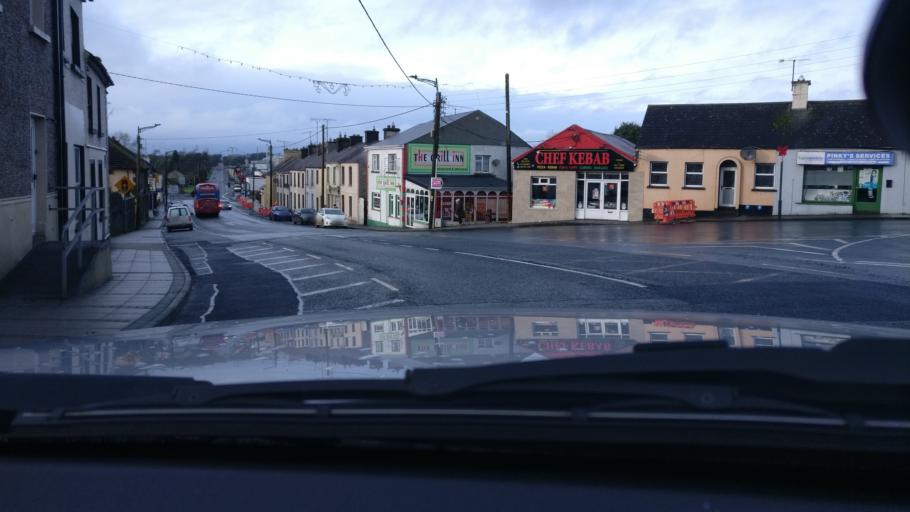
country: IE
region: Leinster
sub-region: An Longfort
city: Edgeworthstown
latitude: 53.6965
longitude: -7.6094
